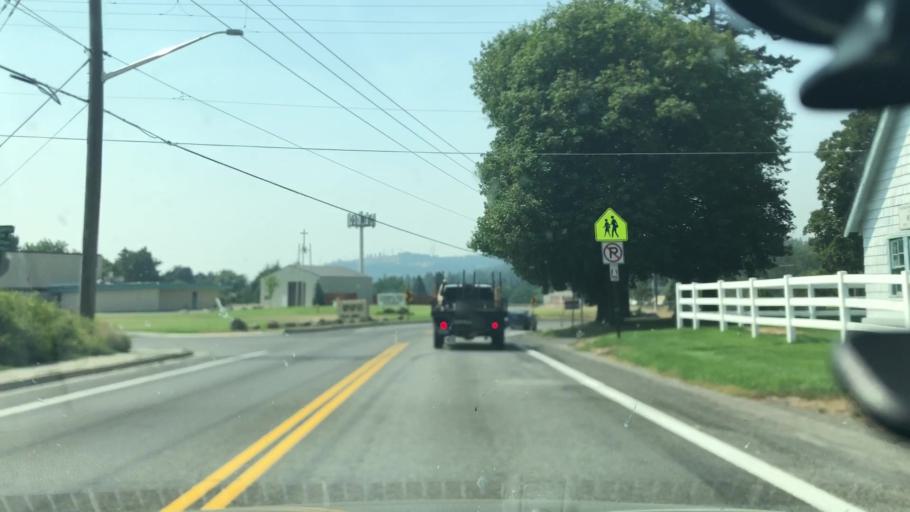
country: US
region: Washington
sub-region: Spokane County
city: Millwood
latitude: 47.6969
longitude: -117.2851
